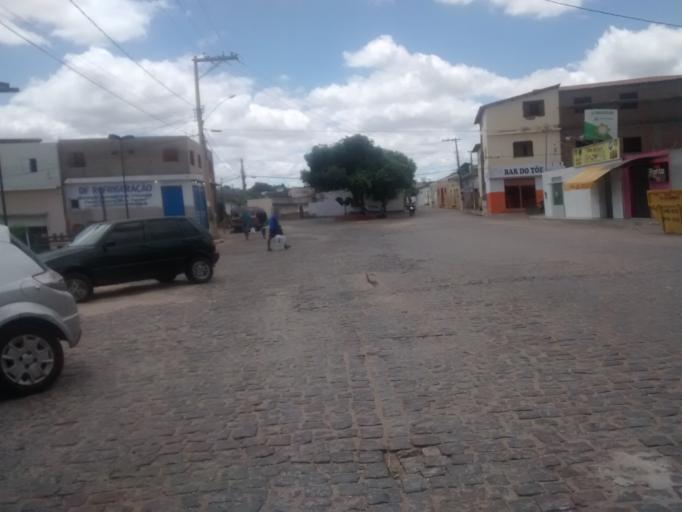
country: BR
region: Bahia
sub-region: Brumado
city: Brumado
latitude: -14.1997
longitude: -41.6694
